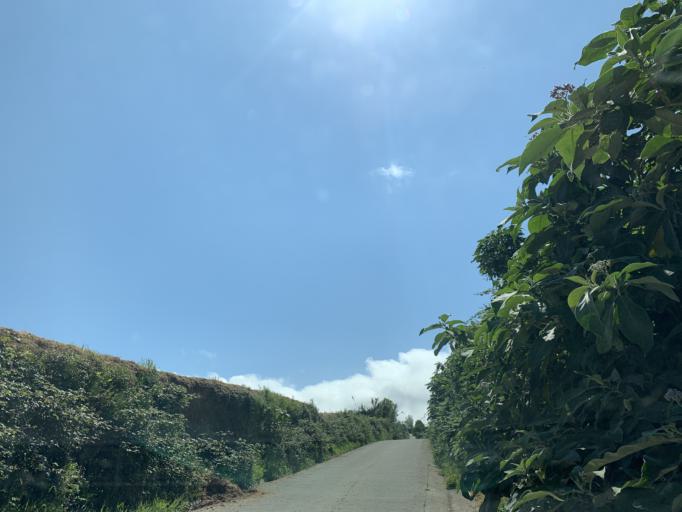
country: PT
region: Azores
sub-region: Ponta Delgada
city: Arrifes
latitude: 37.8630
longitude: -25.7151
